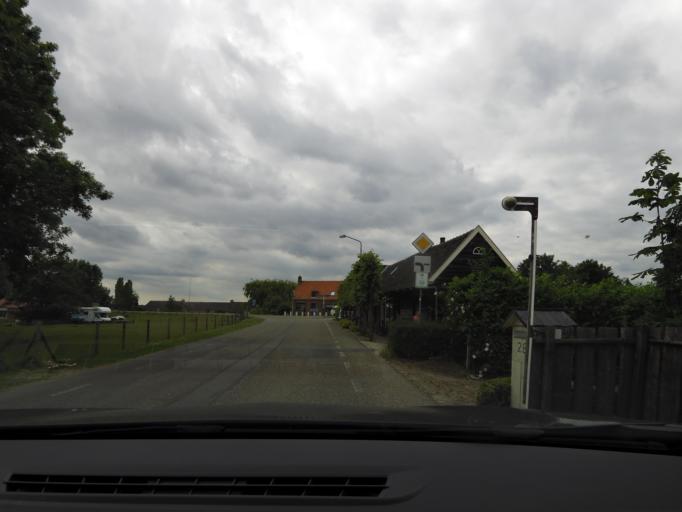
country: NL
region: North Brabant
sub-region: Gemeente Moerdijk
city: Klundert
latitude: 51.6603
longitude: 4.4960
